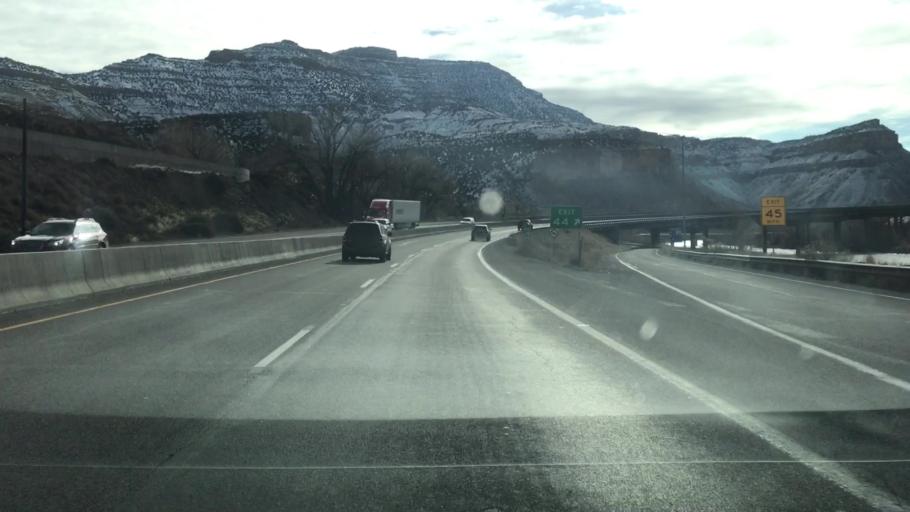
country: US
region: Colorado
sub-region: Mesa County
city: Palisade
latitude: 39.1268
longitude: -108.3236
